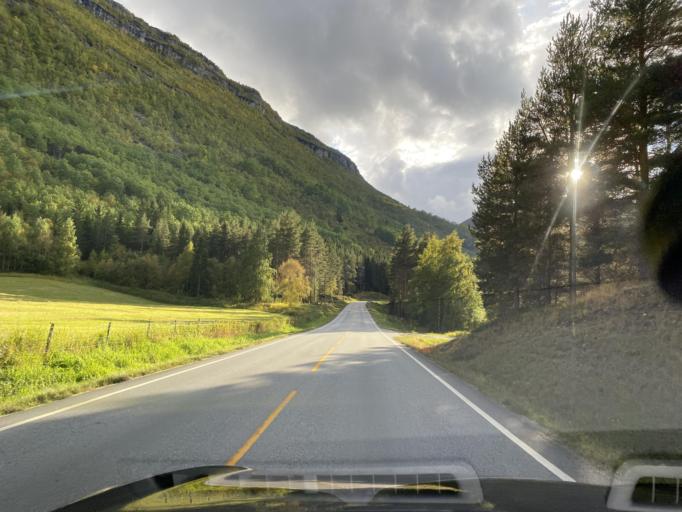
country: NO
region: Oppland
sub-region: Lom
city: Fossbergom
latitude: 61.8106
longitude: 8.4863
